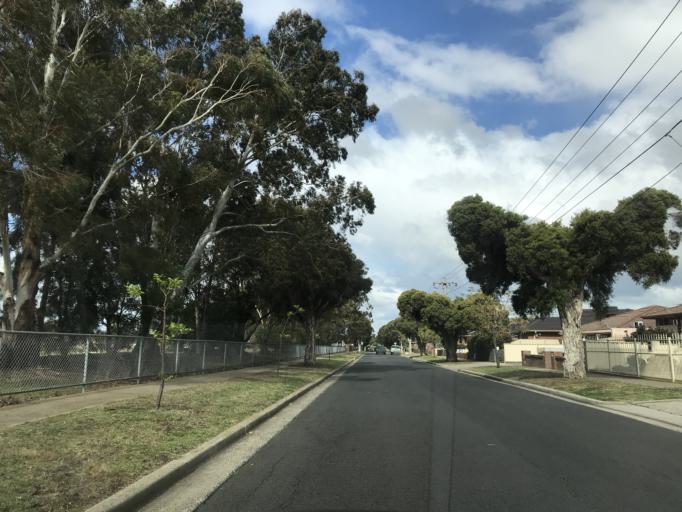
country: AU
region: Victoria
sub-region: Brimbank
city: Sunshine West
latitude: -37.7896
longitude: 144.7939
